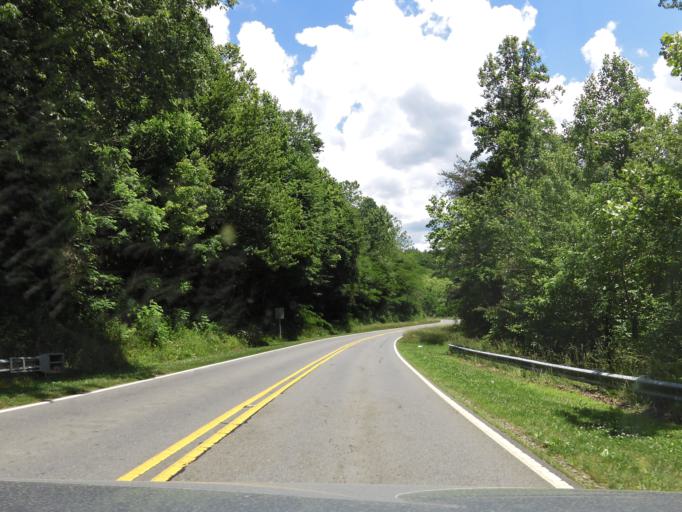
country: US
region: North Carolina
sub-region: Graham County
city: Robbinsville
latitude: 35.3454
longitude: -83.8172
